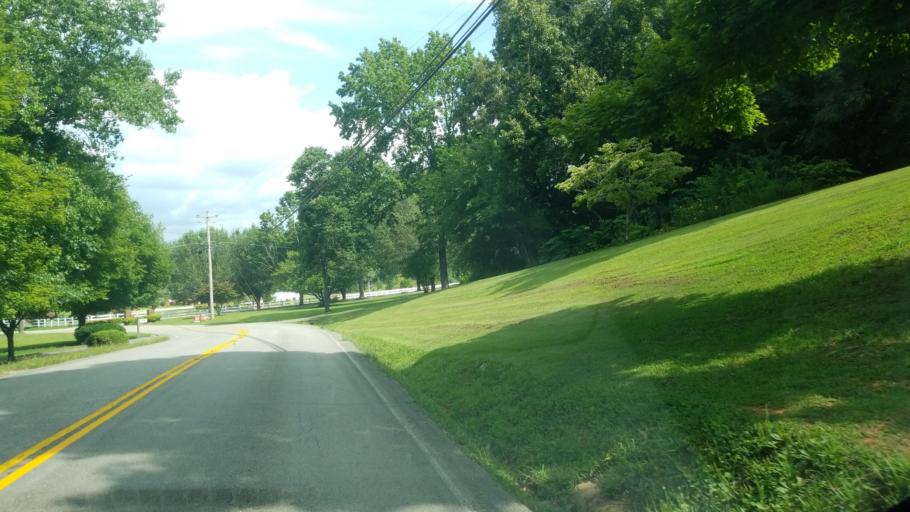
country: US
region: Tennessee
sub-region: Hamilton County
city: Lakesite
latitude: 35.1869
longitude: -85.1039
